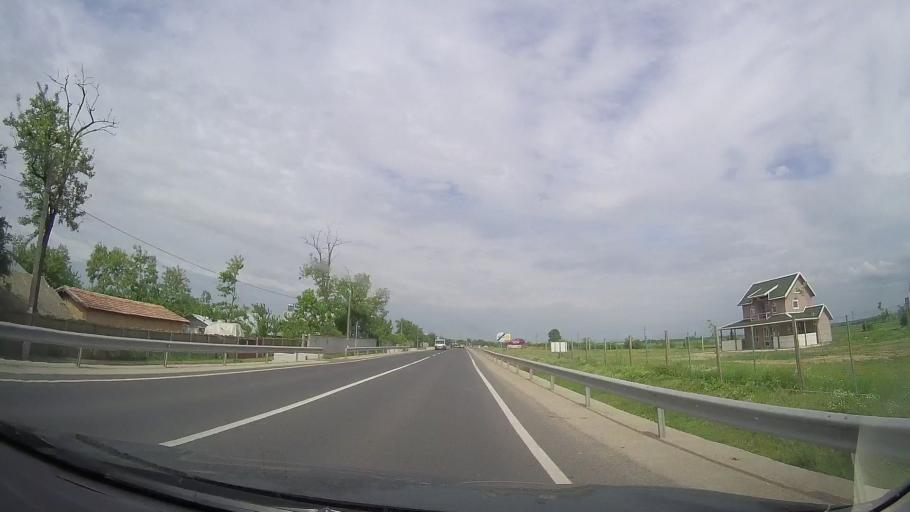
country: RO
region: Teleorman
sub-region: Comuna Nenciulesti
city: Nenciulesti
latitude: 44.0208
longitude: 25.1698
